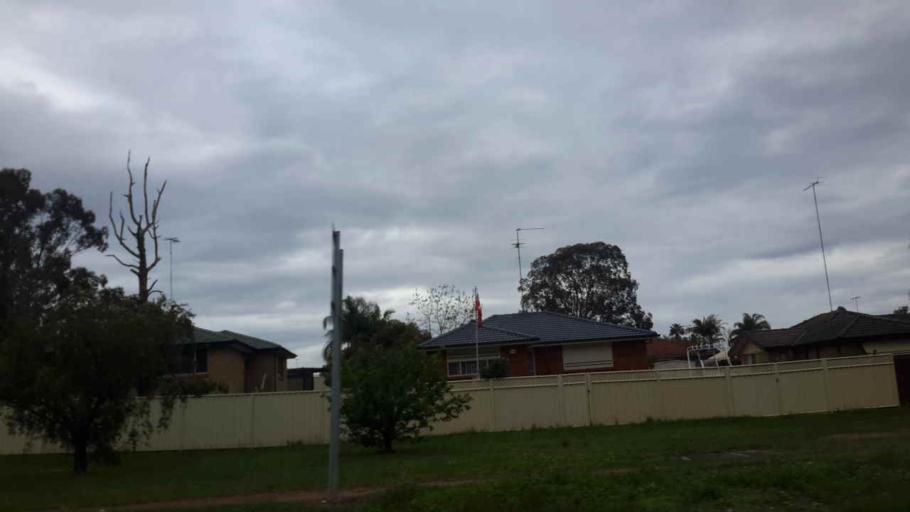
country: AU
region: New South Wales
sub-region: Penrith Municipality
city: Werrington Downs
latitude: -33.7327
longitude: 150.7181
